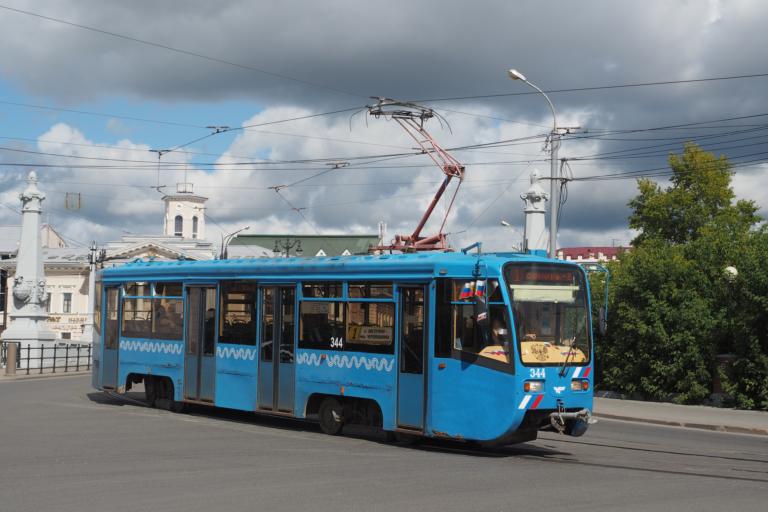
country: RU
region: Tomsk
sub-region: Tomskiy Rayon
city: Tomsk
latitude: 56.4873
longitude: 84.9512
